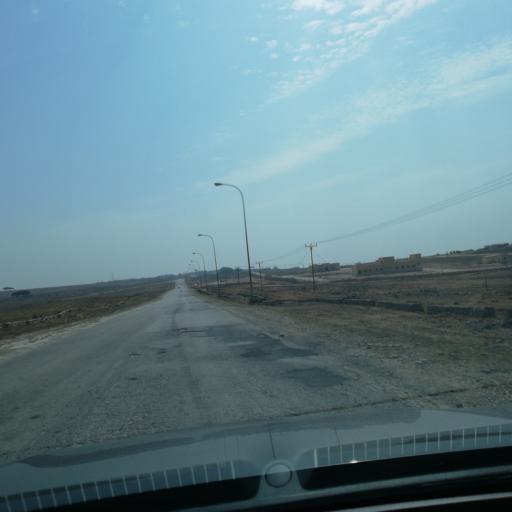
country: OM
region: Zufar
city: Salalah
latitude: 17.2414
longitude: 54.0629
